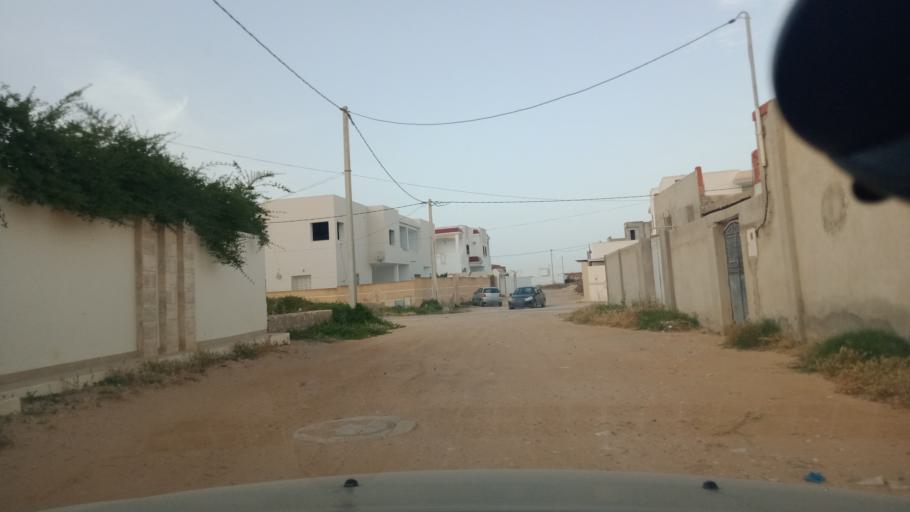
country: TN
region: Safaqis
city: Al Qarmadah
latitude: 34.7909
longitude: 10.7696
